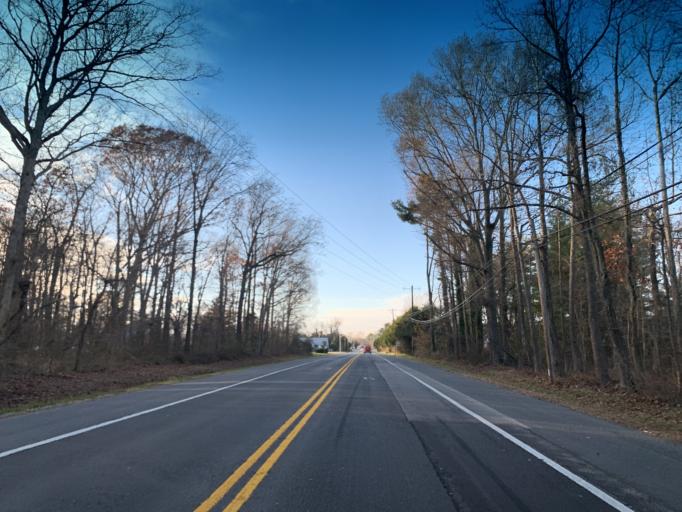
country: US
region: Maryland
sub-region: Queen Anne's County
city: Kingstown
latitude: 39.2028
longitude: -76.0481
